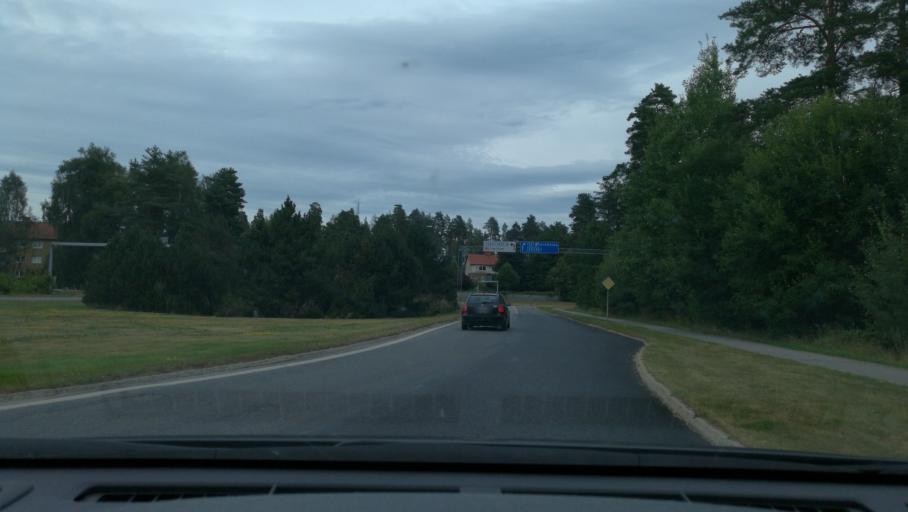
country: SE
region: Soedermanland
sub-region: Katrineholms Kommun
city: Katrineholm
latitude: 58.9865
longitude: 16.2101
